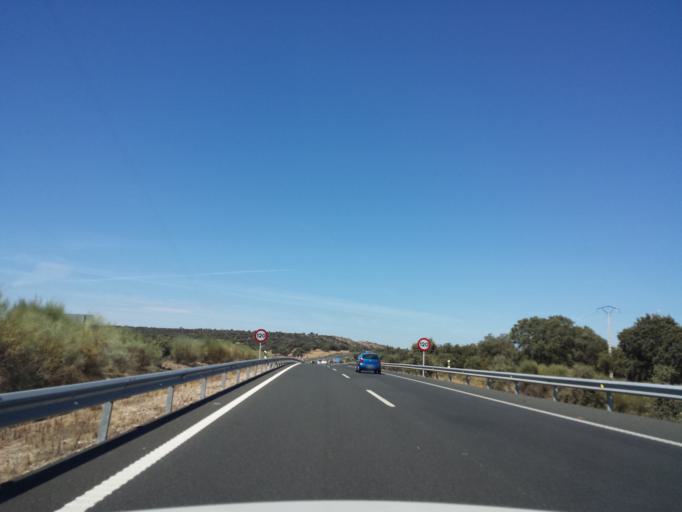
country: ES
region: Extremadura
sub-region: Provincia de Caceres
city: Peraleda de la Mata
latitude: 39.8889
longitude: -5.4848
